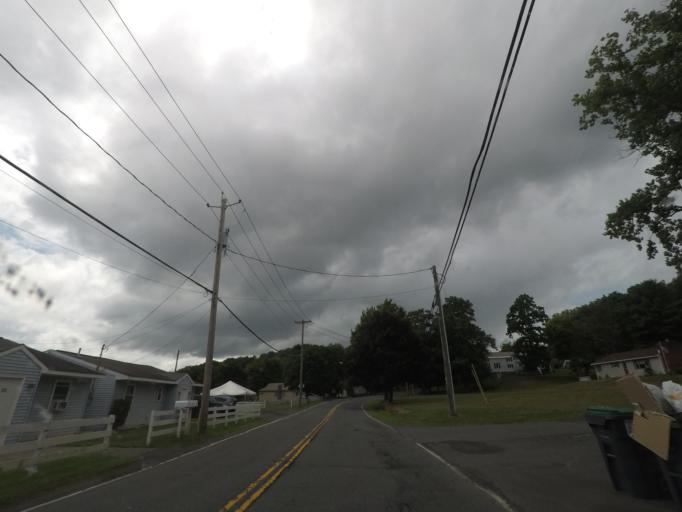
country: US
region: New York
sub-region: Rensselaer County
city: Wynantskill
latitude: 42.6657
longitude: -73.6341
